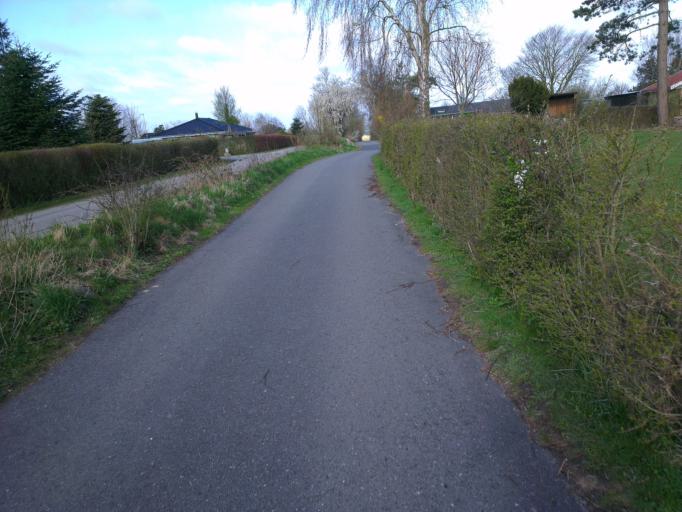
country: DK
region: Capital Region
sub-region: Frederikssund Kommune
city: Jaegerspris
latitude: 55.8340
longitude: 11.9562
